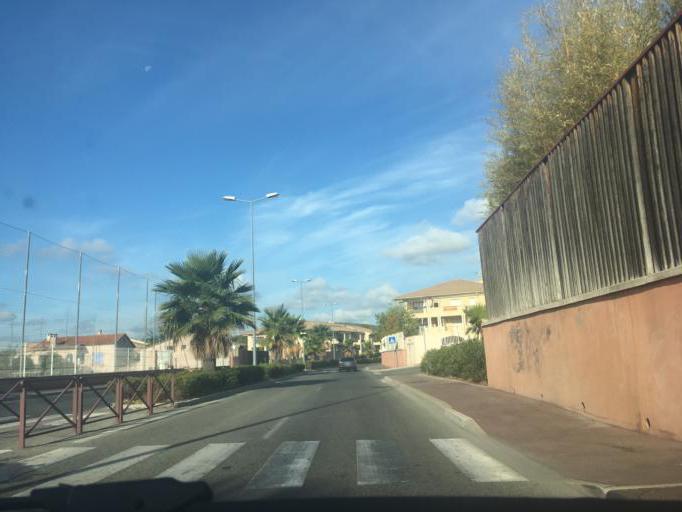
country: FR
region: Provence-Alpes-Cote d'Azur
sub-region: Departement du Var
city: Draguignan
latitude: 43.5297
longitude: 6.4680
